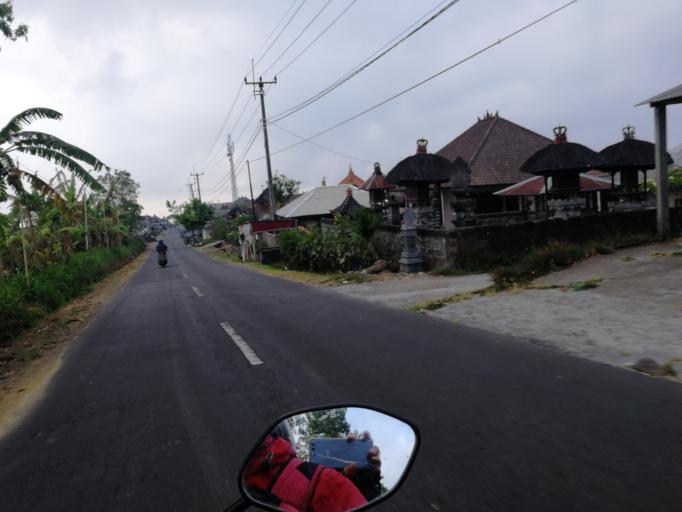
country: ID
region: Bali
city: Banjar Kedisan
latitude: -8.2443
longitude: 115.2443
